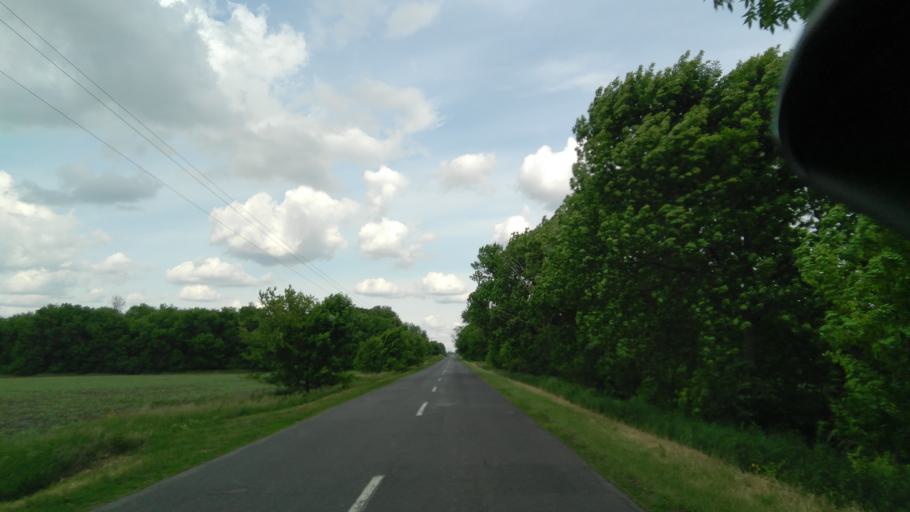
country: HU
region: Bekes
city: Battonya
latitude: 46.2944
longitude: 20.9746
